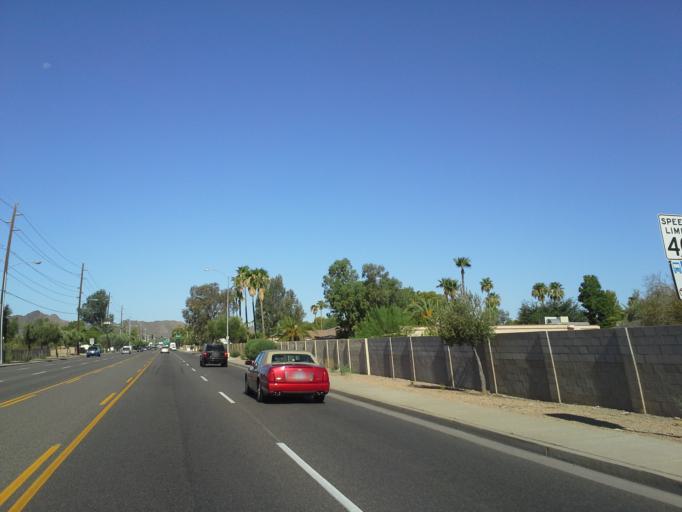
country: US
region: Arizona
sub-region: Maricopa County
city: Paradise Valley
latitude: 33.5827
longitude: -112.0005
